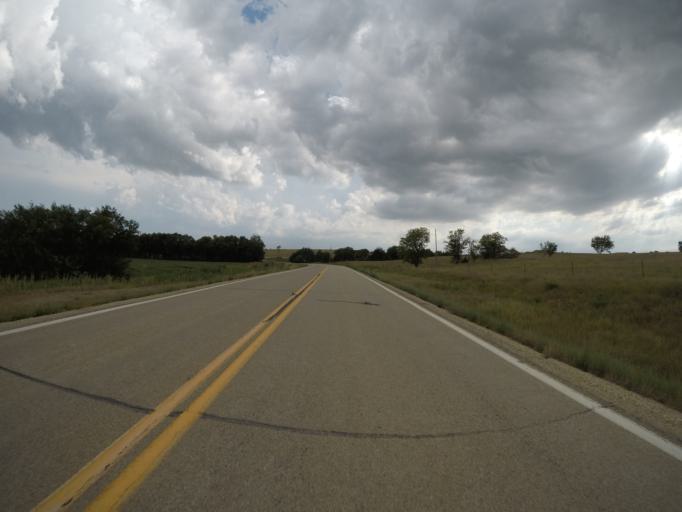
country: US
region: Kansas
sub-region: Marshall County
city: Blue Rapids
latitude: 39.4688
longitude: -96.8333
